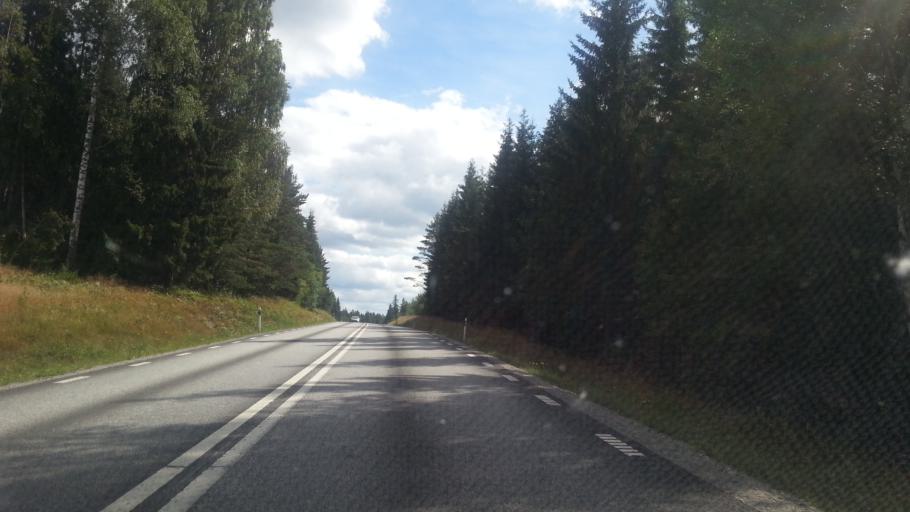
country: SE
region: OErebro
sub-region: Lindesbergs Kommun
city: Stora
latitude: 59.6493
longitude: 15.1174
